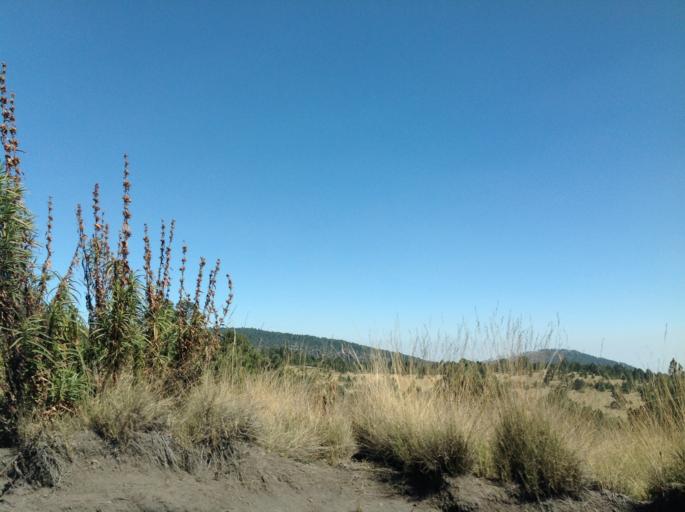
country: MX
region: Mexico
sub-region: Amecameca
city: San Diego Huehuecalco
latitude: 19.1068
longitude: -98.6453
